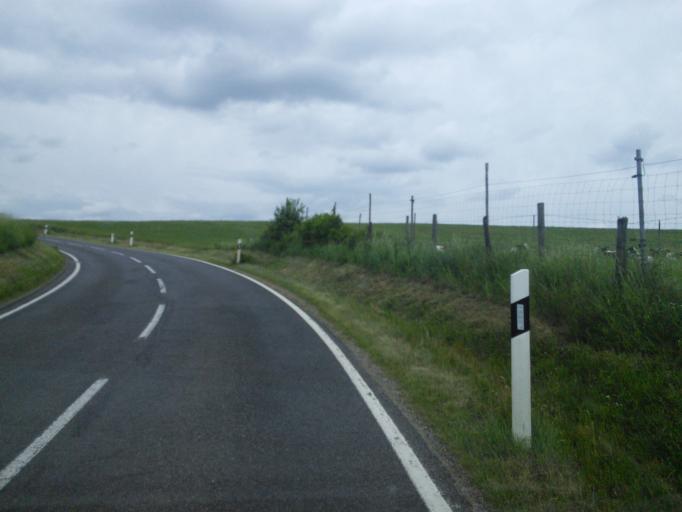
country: DE
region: Rheinland-Pfalz
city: Kirchsahr
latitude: 50.5530
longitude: 6.8985
